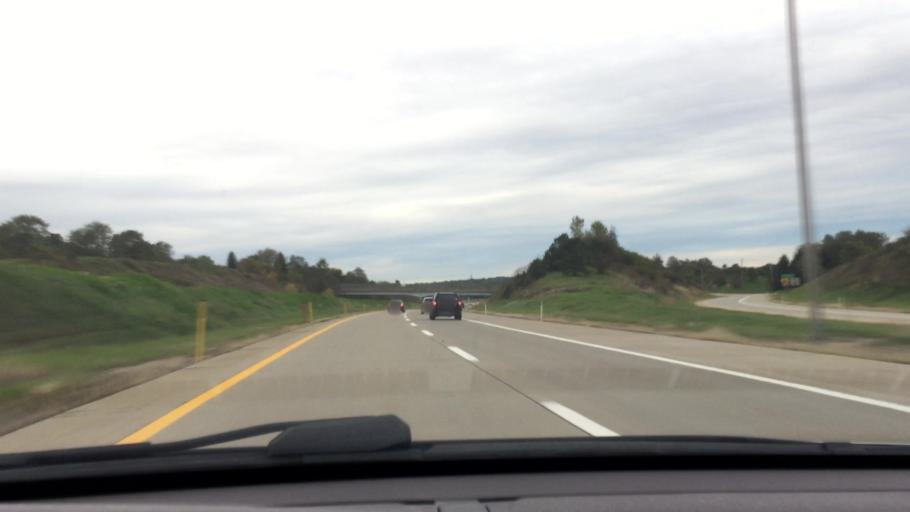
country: US
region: Pennsylvania
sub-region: Lawrence County
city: Oakland
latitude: 40.9670
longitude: -80.4000
